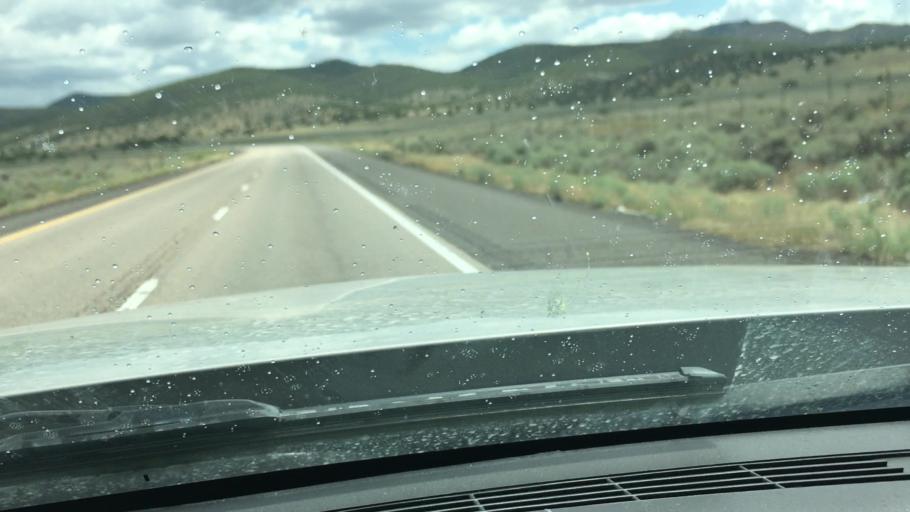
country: US
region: Utah
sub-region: Beaver County
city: Beaver
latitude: 38.1987
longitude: -112.6465
